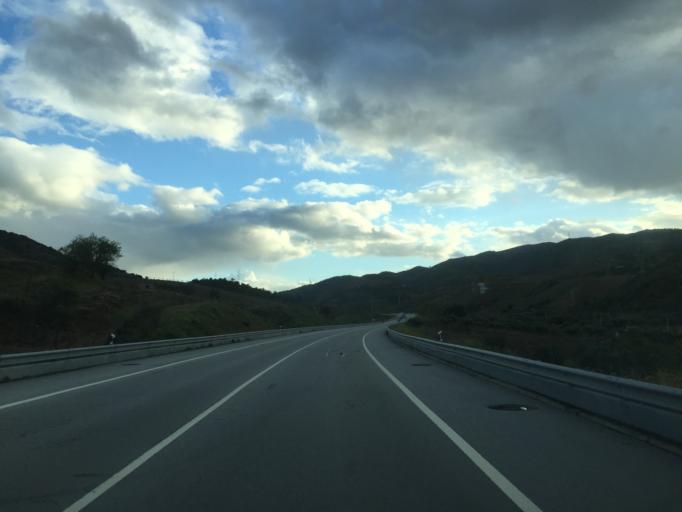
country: PT
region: Guarda
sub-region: Vila Nova de Foz Coa
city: Vila Nova de Foz Coa
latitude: 41.1089
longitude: -7.1368
